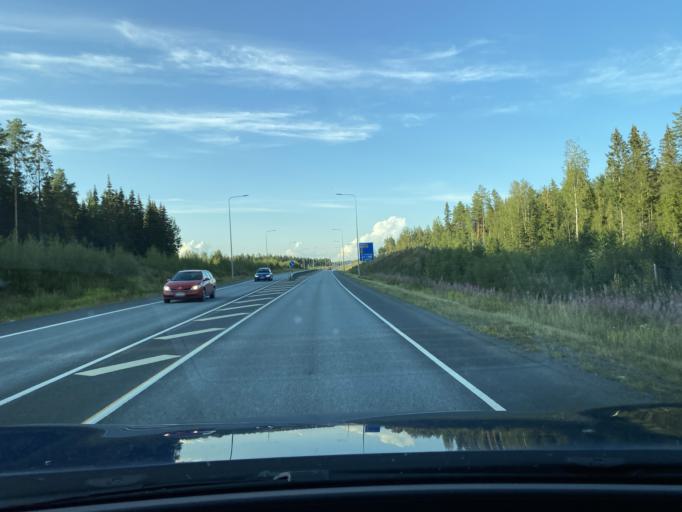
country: FI
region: Southern Ostrobothnia
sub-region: Seinaejoki
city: Seinaejoki
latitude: 62.6853
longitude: 22.8017
